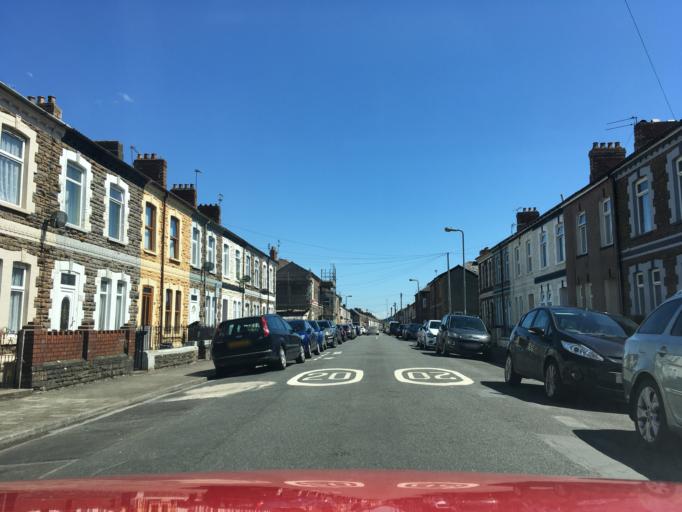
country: GB
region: Wales
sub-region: Cardiff
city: Cardiff
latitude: 51.4826
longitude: -3.1516
